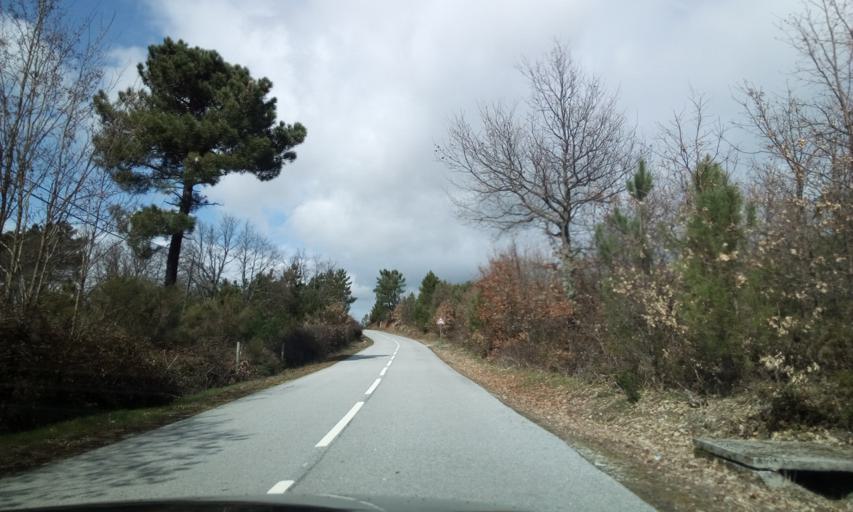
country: PT
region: Guarda
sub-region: Fornos de Algodres
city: Fornos de Algodres
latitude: 40.6369
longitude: -7.5476
